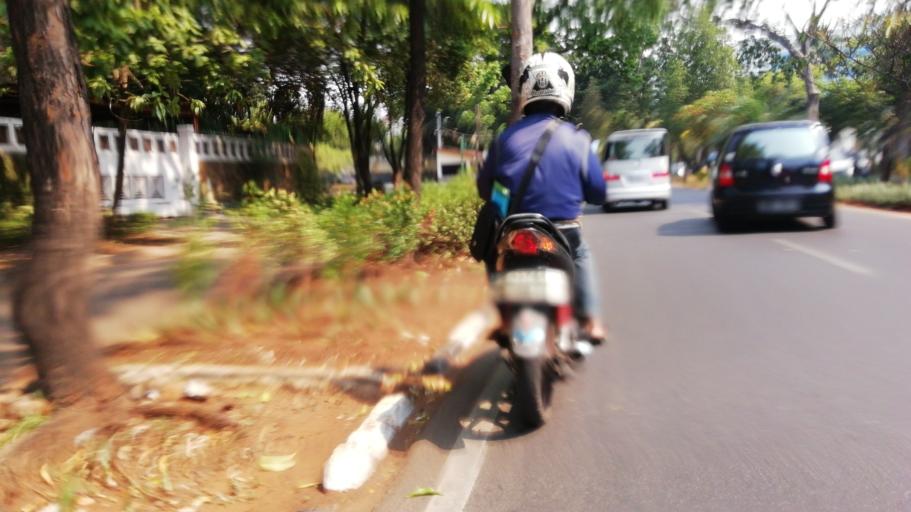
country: ID
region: Jakarta Raya
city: Jakarta
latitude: -6.2351
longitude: 106.8015
